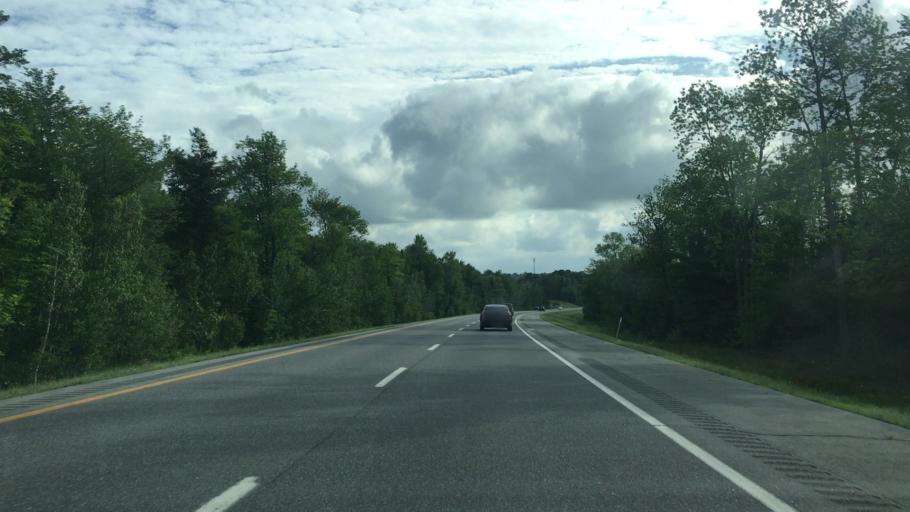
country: US
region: Maine
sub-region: Somerset County
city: Palmyra
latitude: 44.8187
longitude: -69.3350
